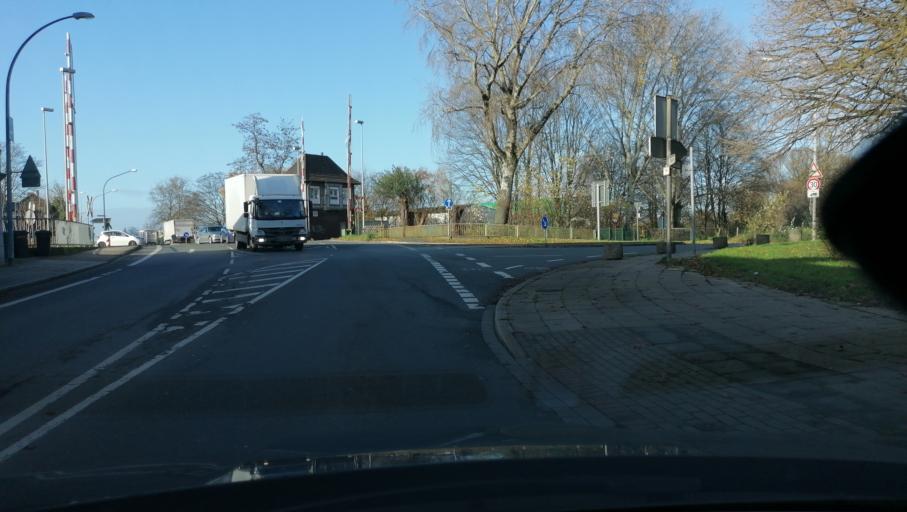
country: DE
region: North Rhine-Westphalia
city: Bochum-Hordel
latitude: 51.5449
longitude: 7.1808
